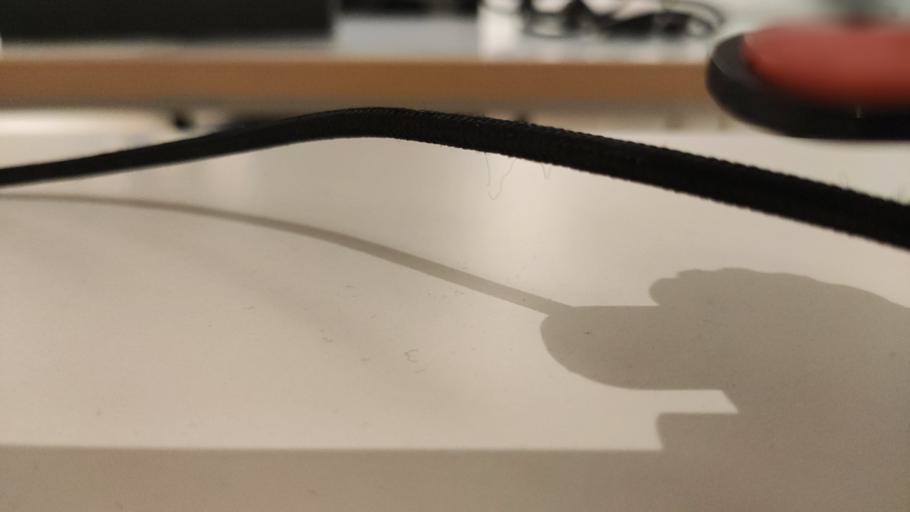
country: RU
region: Kaluga
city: Zhukovo
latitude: 55.1400
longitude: 36.7791
